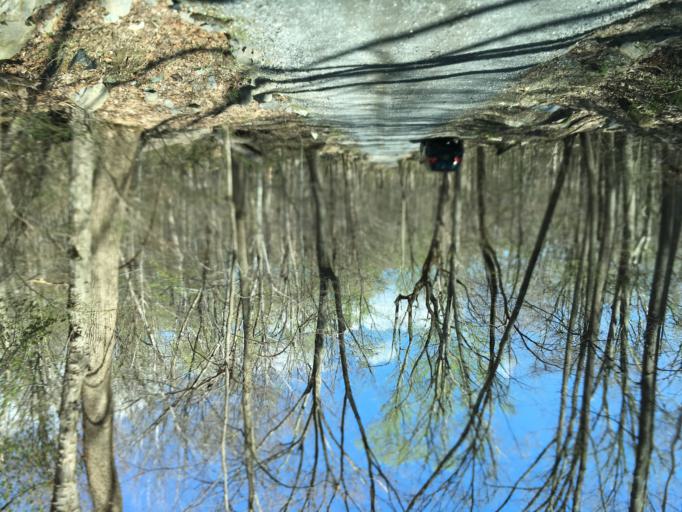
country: US
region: Maryland
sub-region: Washington County
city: Highfield-Cascade
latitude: 39.6536
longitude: -77.4776
